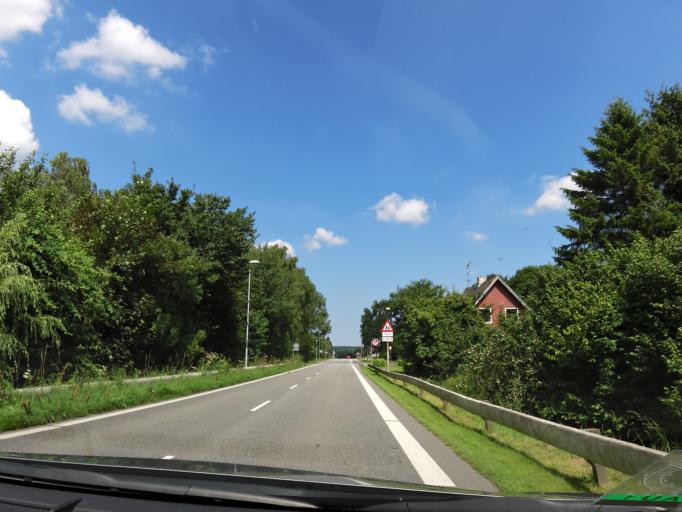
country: DK
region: South Denmark
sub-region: Assens Kommune
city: Arup
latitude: 55.3724
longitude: 10.0451
